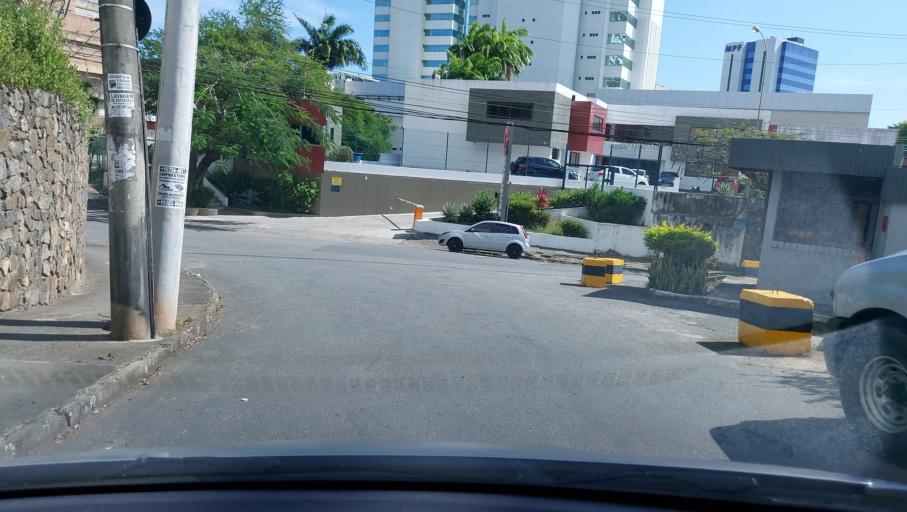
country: BR
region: Bahia
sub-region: Salvador
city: Salvador
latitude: -12.9643
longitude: -38.4386
